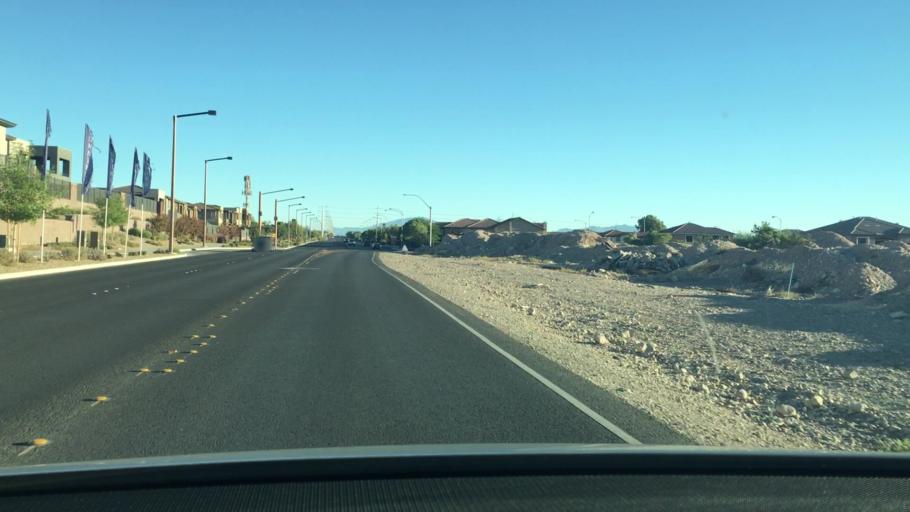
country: US
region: Nevada
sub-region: Clark County
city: Summerlin South
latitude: 36.0762
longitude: -115.3157
